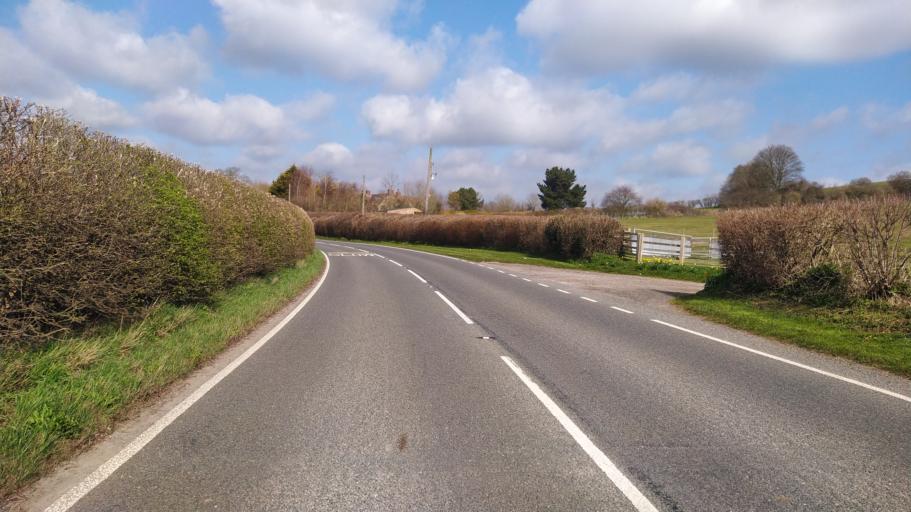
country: GB
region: England
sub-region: Dorset
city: Beaminster
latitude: 50.7719
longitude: -2.7323
